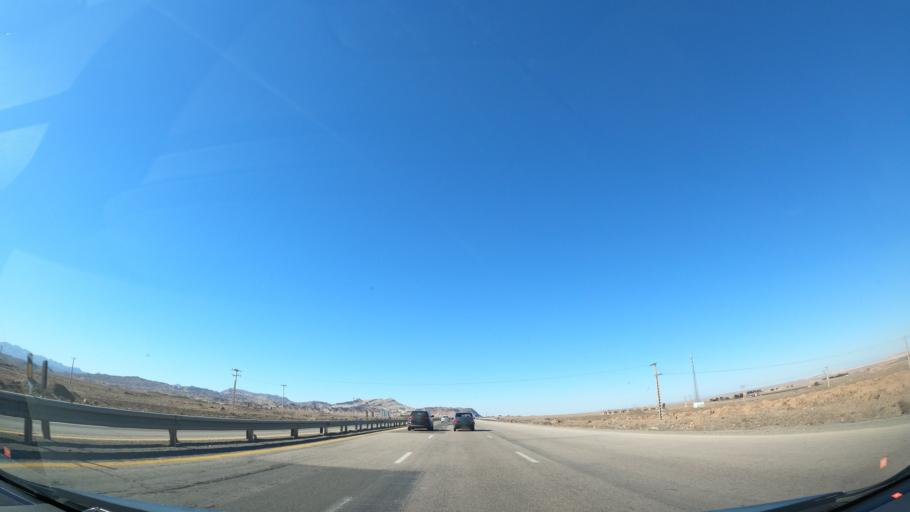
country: IR
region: Isfahan
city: Aran Bidgol
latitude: 34.3848
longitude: 51.2185
